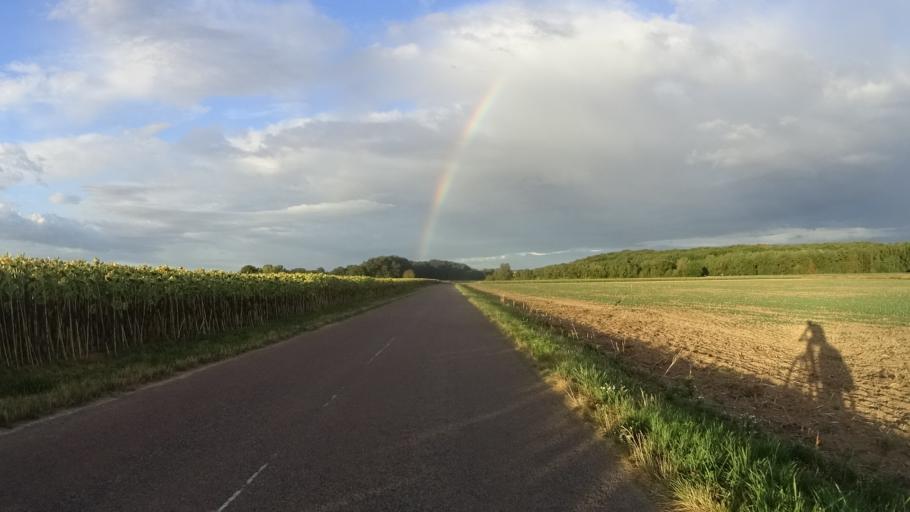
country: FR
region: Bourgogne
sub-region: Departement de la Cote-d'Or
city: Seurre
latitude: 46.9630
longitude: 5.0793
